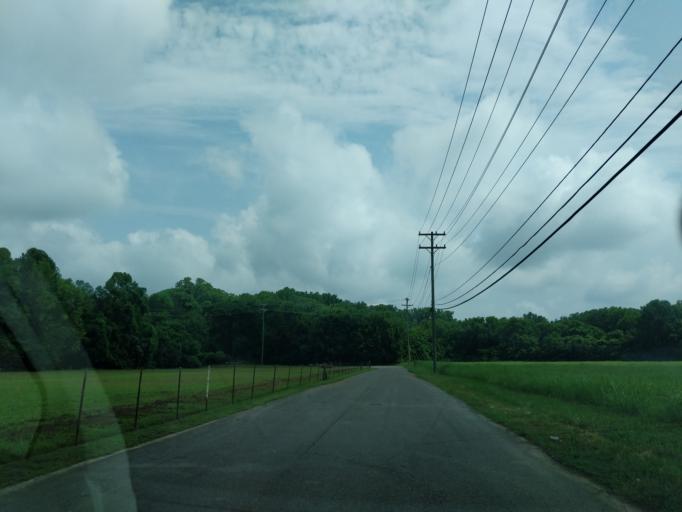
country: US
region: Tennessee
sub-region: Davidson County
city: Lakewood
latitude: 36.1886
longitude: -86.6121
